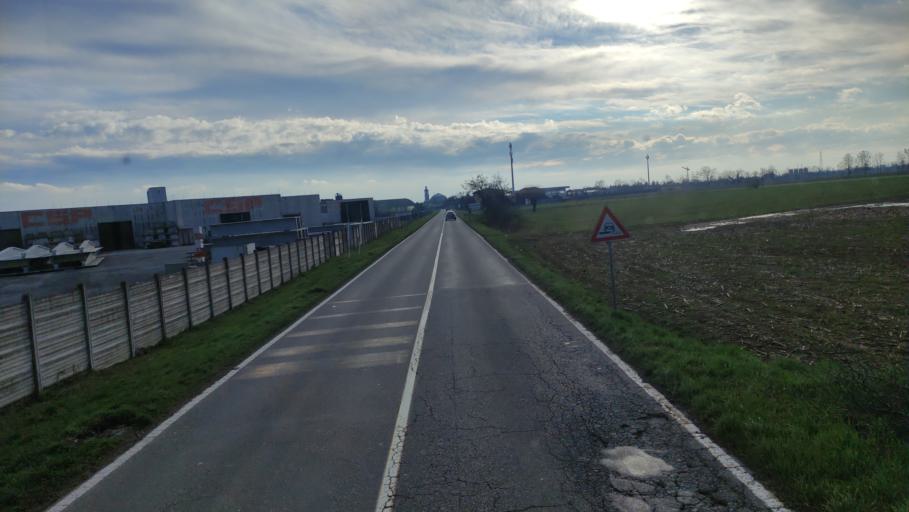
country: IT
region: Lombardy
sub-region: Provincia di Bergamo
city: Ghisalba
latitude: 45.6049
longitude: 9.7624
